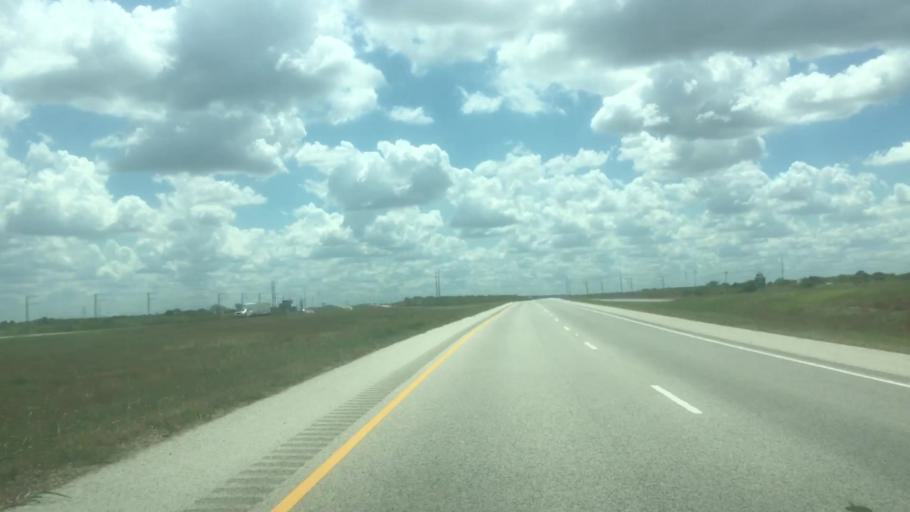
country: US
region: Texas
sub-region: Caldwell County
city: Uhland
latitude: 30.0193
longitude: -97.6877
